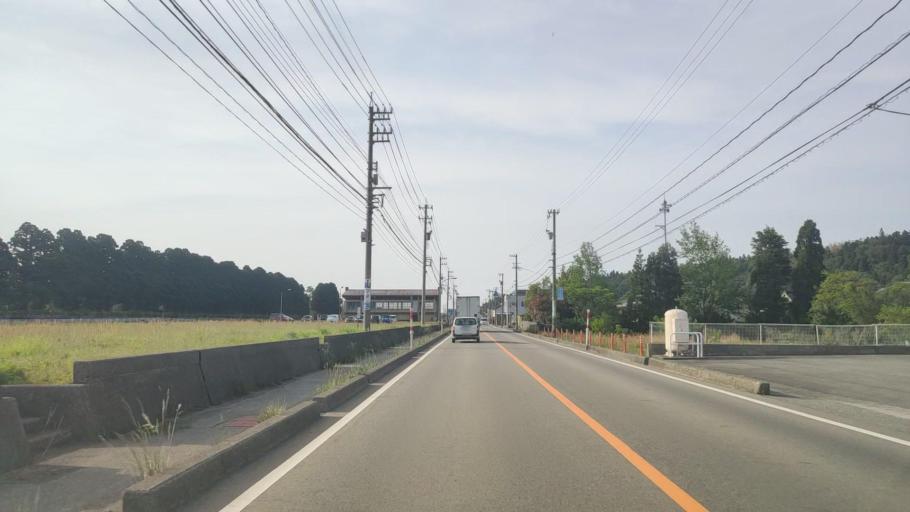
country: JP
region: Toyama
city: Yatsuomachi-higashikumisaka
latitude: 36.5695
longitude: 137.2102
